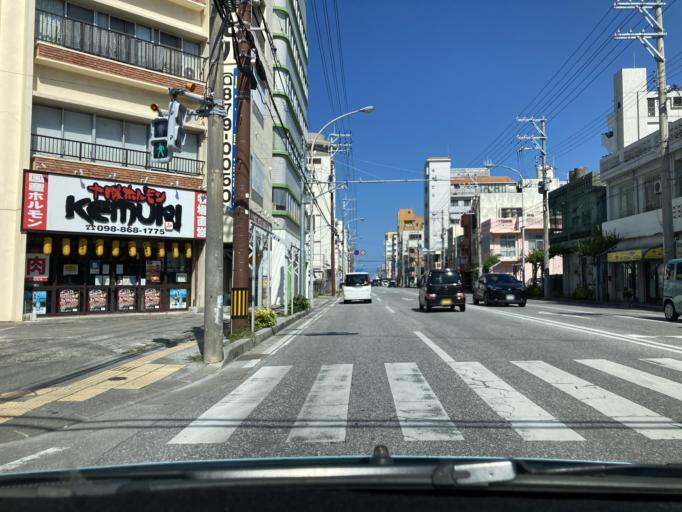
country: JP
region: Okinawa
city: Naha-shi
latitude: 26.2388
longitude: 127.6816
